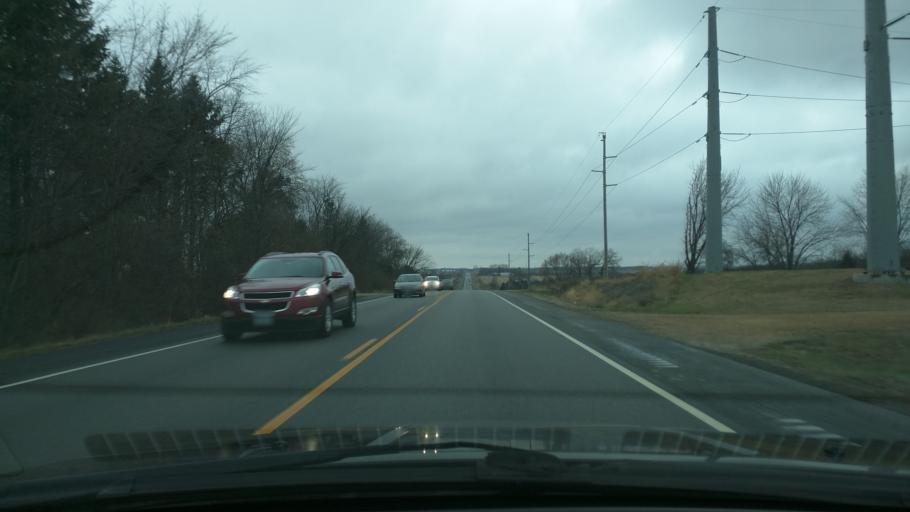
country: US
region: Minnesota
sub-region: Dakota County
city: Hastings
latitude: 44.7384
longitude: -92.9126
